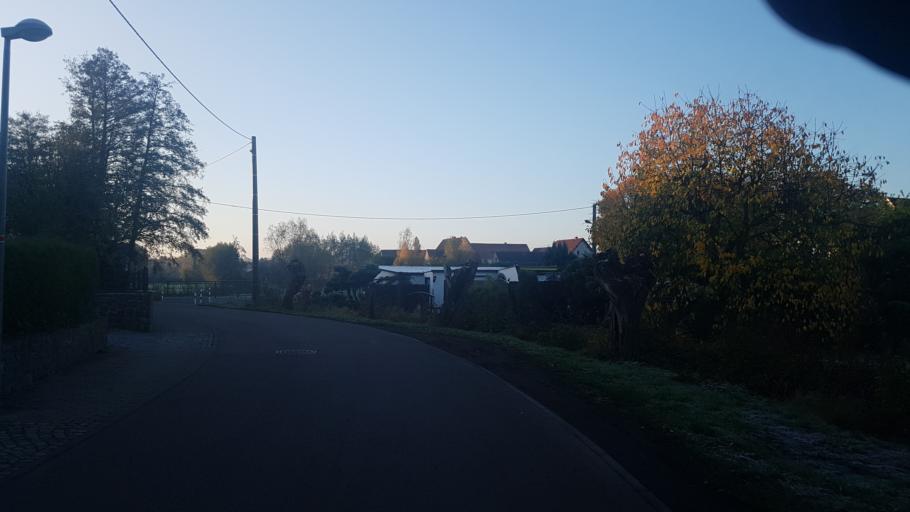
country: DE
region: Saxony
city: Schildau
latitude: 51.4433
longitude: 12.9694
